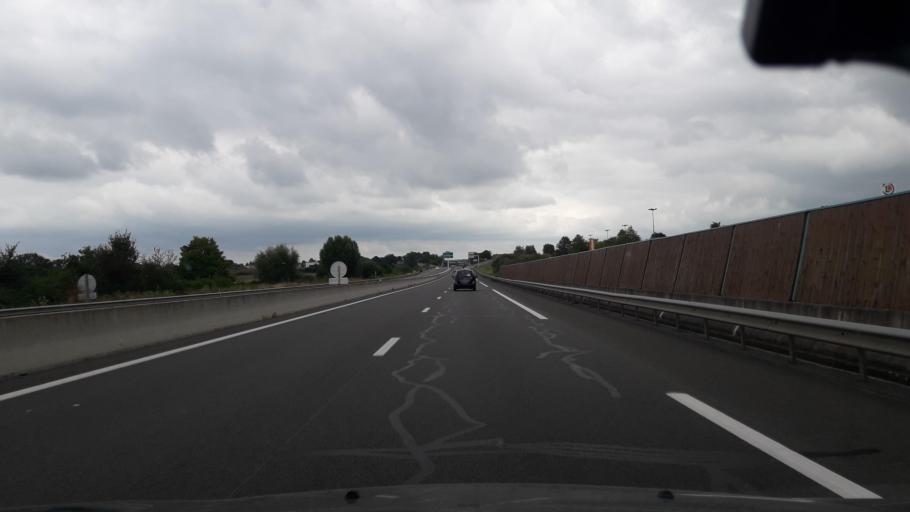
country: FR
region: Auvergne
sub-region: Departement de l'Allier
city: Domerat
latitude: 46.3666
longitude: 2.5611
